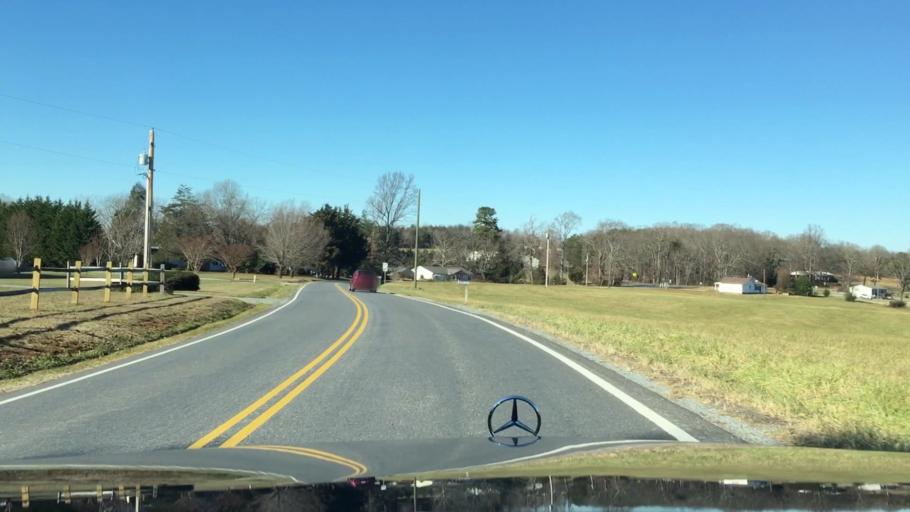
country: US
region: Virginia
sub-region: Pittsylvania County
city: Motley
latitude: 37.2022
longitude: -79.4273
